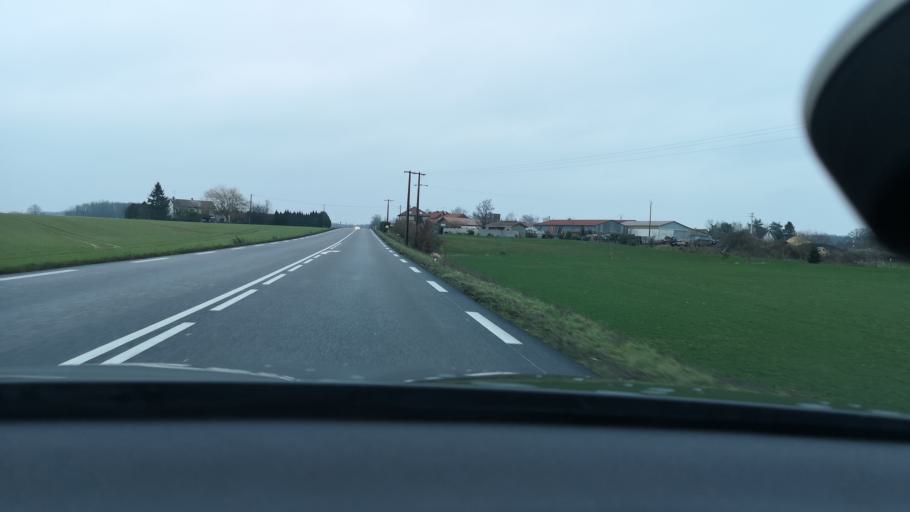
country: FR
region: Bourgogne
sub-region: Departement de la Cote-d'Or
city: Seurre
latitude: 46.9587
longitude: 5.1675
